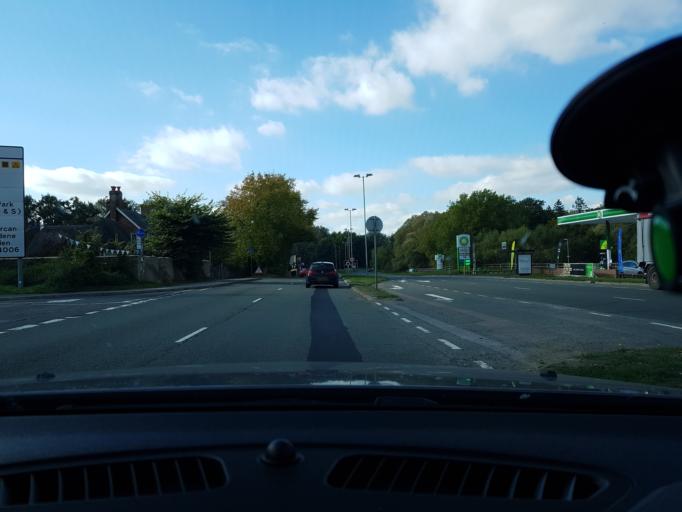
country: GB
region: England
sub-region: Borough of Swindon
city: Chiseldon
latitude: 51.5446
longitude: -1.7420
